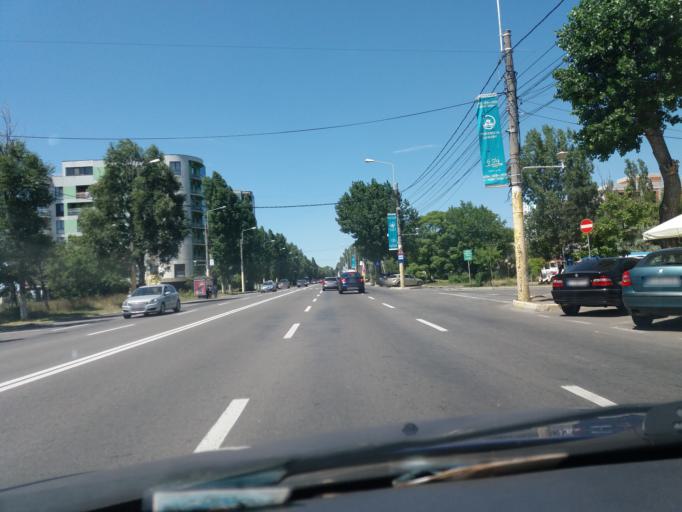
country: RO
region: Constanta
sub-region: Municipiul Constanta
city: Palazu Mare
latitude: 44.2416
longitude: 28.6210
